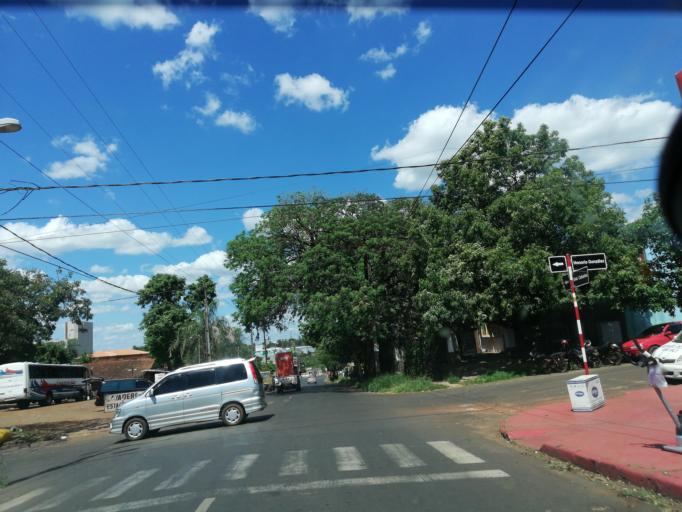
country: PY
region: Itapua
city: Encarnacion
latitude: -27.3391
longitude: -55.8597
